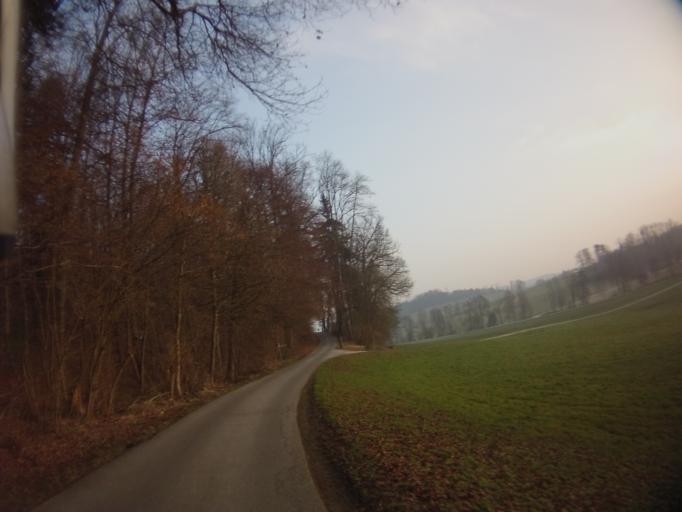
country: CH
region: Zurich
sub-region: Bezirk Affoltern
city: Knonau
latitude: 47.2220
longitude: 8.4464
